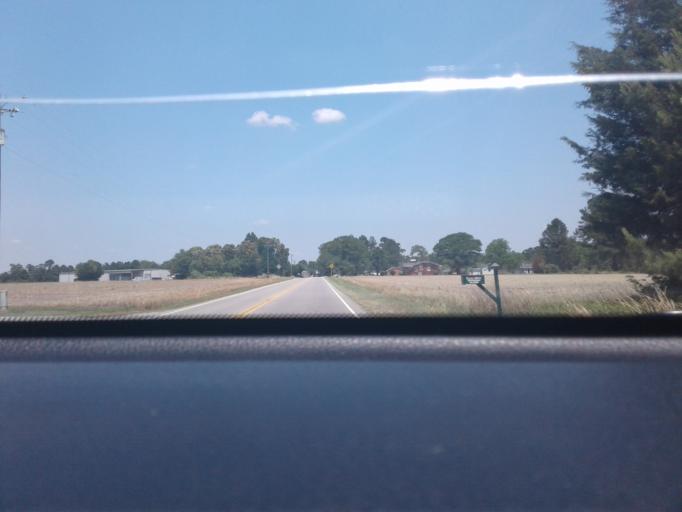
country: US
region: North Carolina
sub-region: Harnett County
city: Dunn
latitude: 35.3359
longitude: -78.5896
